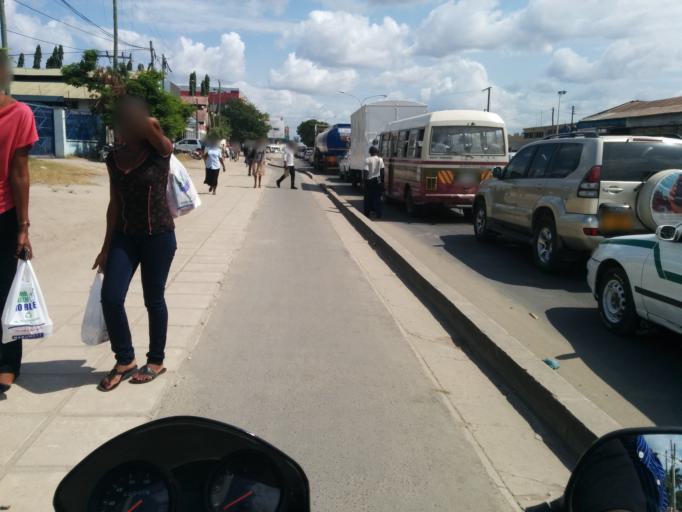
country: TZ
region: Dar es Salaam
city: Dar es Salaam
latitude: -6.8278
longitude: 39.2760
